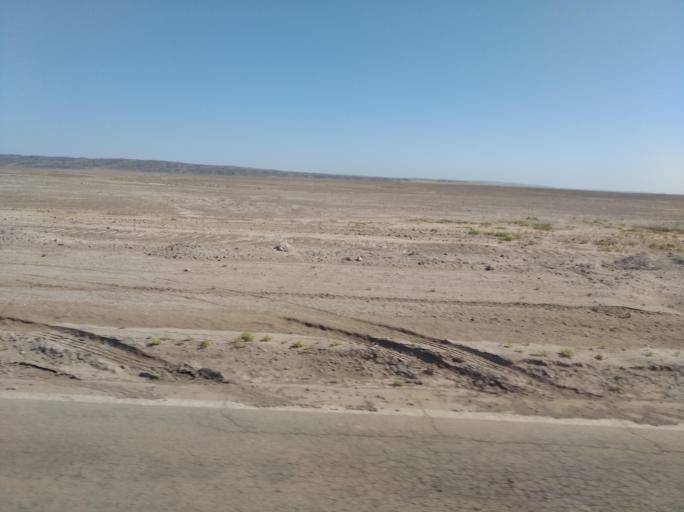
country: CL
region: Atacama
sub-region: Provincia de Copiapo
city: Copiapo
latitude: -27.3280
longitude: -70.7975
